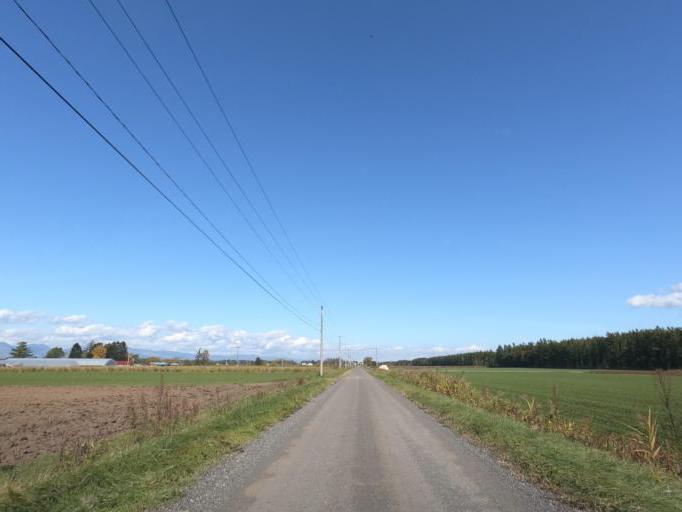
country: JP
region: Hokkaido
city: Otofuke
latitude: 43.0799
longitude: 143.2607
